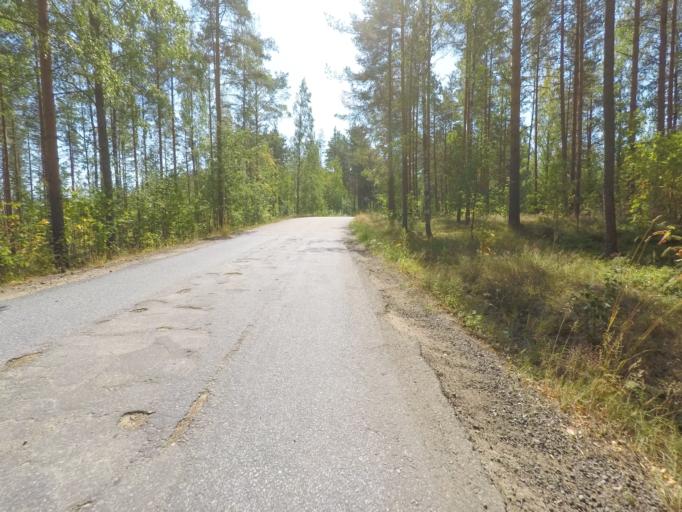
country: FI
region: Southern Savonia
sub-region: Mikkeli
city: Puumala
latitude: 61.4201
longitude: 28.0932
